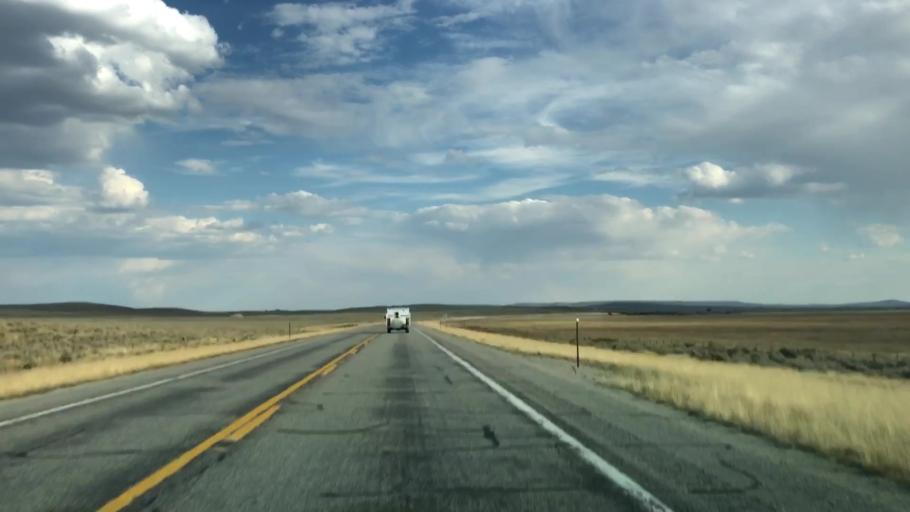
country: US
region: Wyoming
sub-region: Sublette County
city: Pinedale
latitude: 43.0367
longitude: -110.1342
